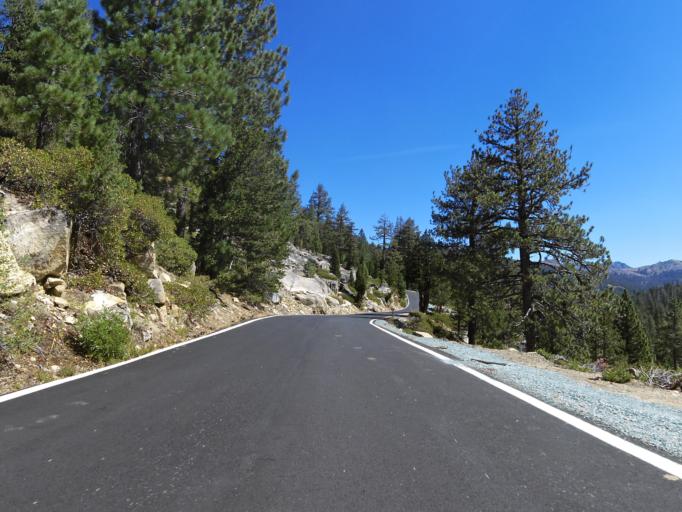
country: US
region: Nevada
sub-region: Douglas County
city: Gardnerville Ranchos
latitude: 38.5459
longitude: -119.8708
